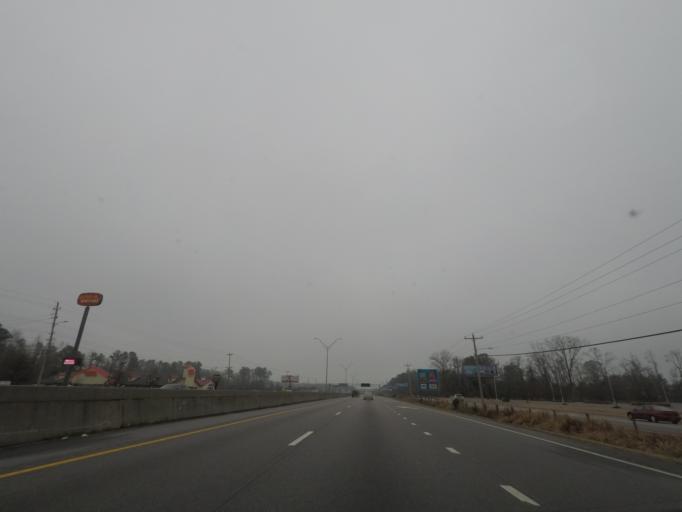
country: US
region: North Carolina
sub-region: Robeson County
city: Lumberton
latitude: 34.6637
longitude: -79.0081
